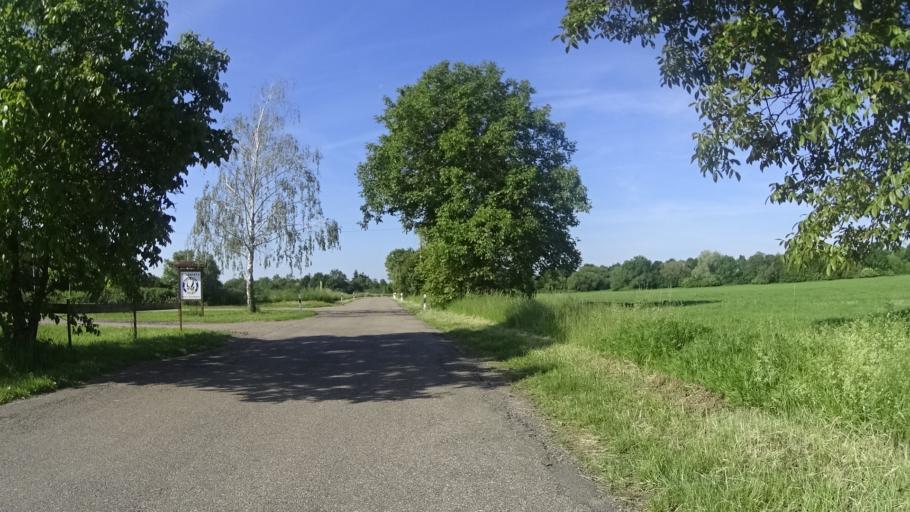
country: DE
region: Baden-Wuerttemberg
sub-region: Freiburg Region
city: Kehl
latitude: 48.5625
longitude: 7.8416
